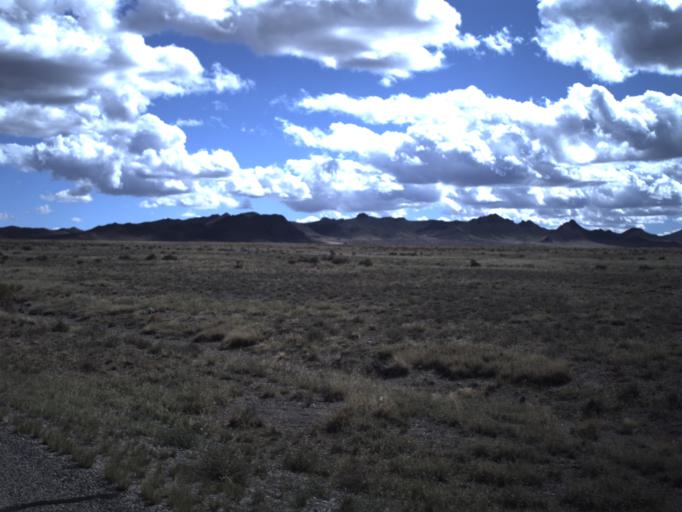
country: US
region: Utah
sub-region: Beaver County
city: Milford
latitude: 38.4513
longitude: -113.3482
